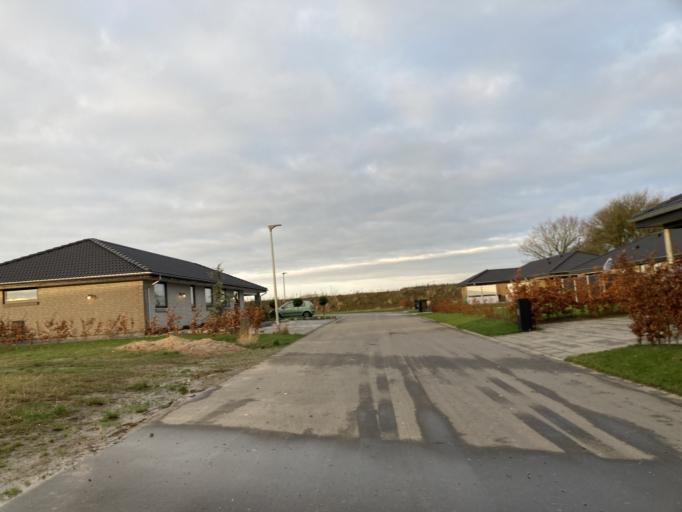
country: DK
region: South Denmark
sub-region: Kolding Kommune
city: Sonder Bjert
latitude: 55.4652
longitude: 9.5652
